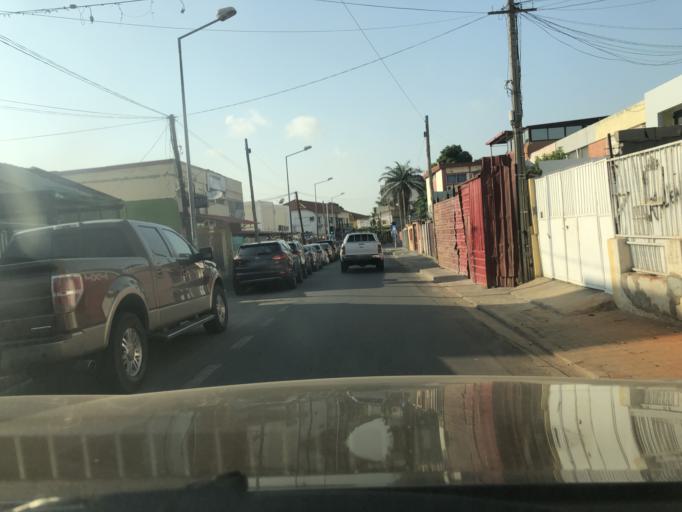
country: AO
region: Luanda
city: Luanda
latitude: -8.8266
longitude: 13.2521
